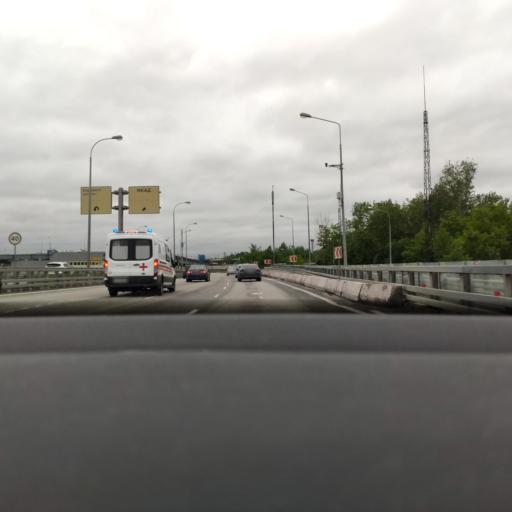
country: RU
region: Moscow
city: Ryazanskiy
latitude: 55.7532
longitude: 37.7397
